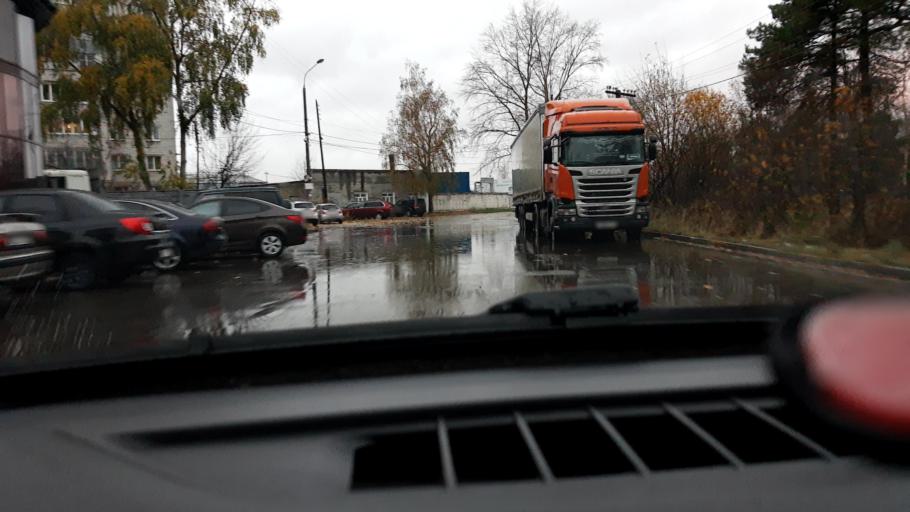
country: RU
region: Nizjnij Novgorod
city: Gorbatovka
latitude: 56.2922
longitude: 43.8412
